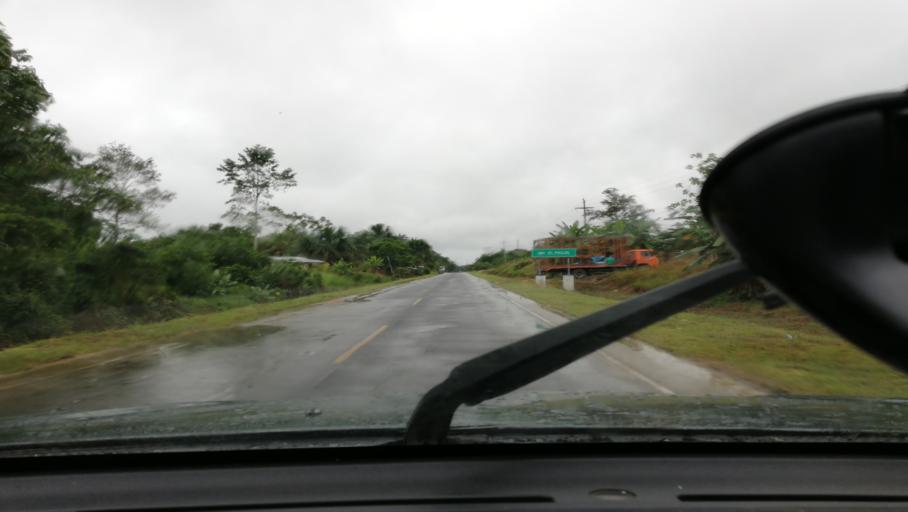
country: PE
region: Loreto
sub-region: Provincia de Maynas
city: San Juan
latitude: -4.0468
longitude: -73.4378
